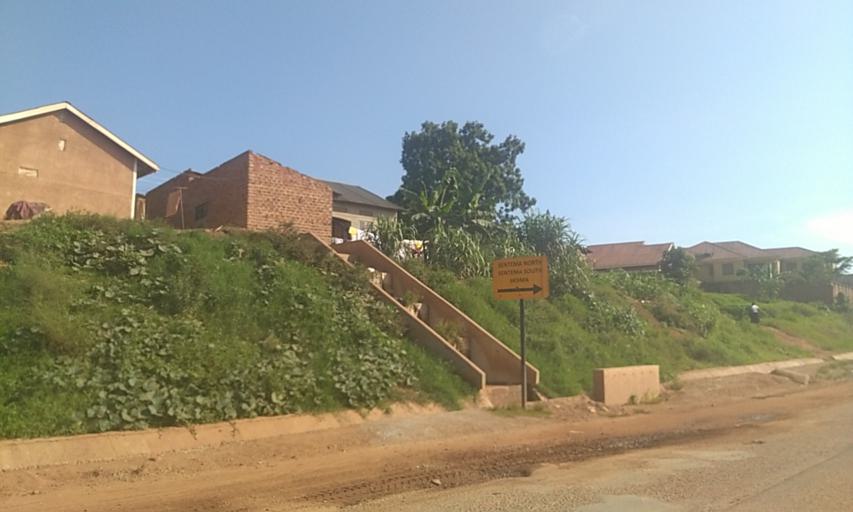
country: UG
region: Central Region
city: Kampala Central Division
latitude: 0.3285
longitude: 32.5250
